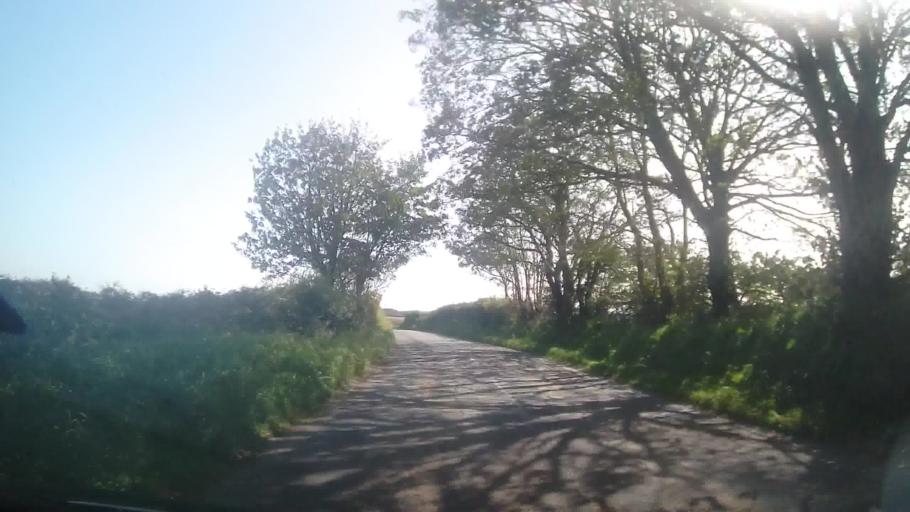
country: GB
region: Wales
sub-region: Pembrokeshire
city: Mathry
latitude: 51.9400
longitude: -5.0461
